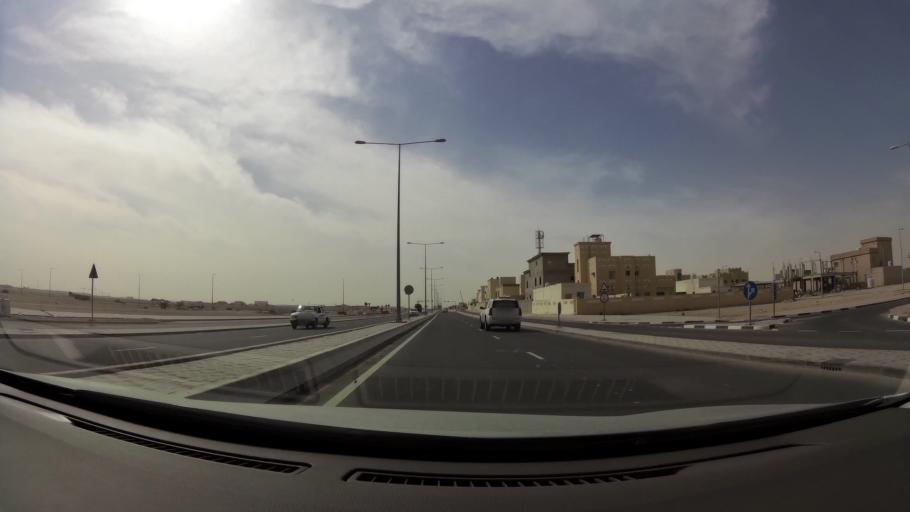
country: QA
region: Baladiyat ar Rayyan
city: Ar Rayyan
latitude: 25.3271
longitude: 51.3807
